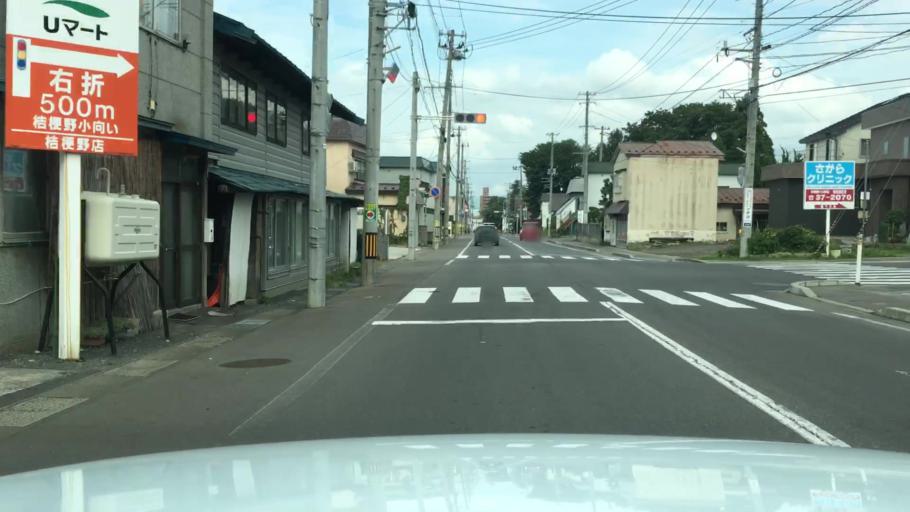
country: JP
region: Aomori
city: Hirosaki
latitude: 40.5962
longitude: 140.4641
